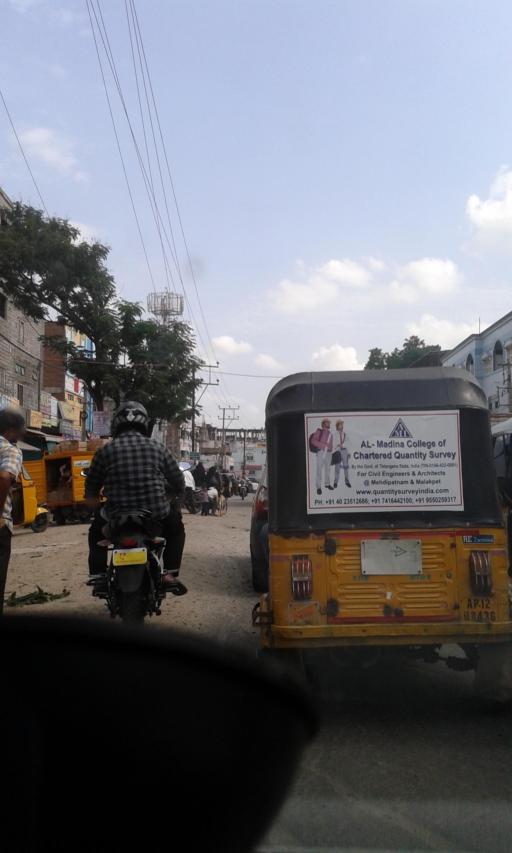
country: IN
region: Telangana
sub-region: Rangareddi
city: Balapur
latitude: 17.3227
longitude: 78.4803
